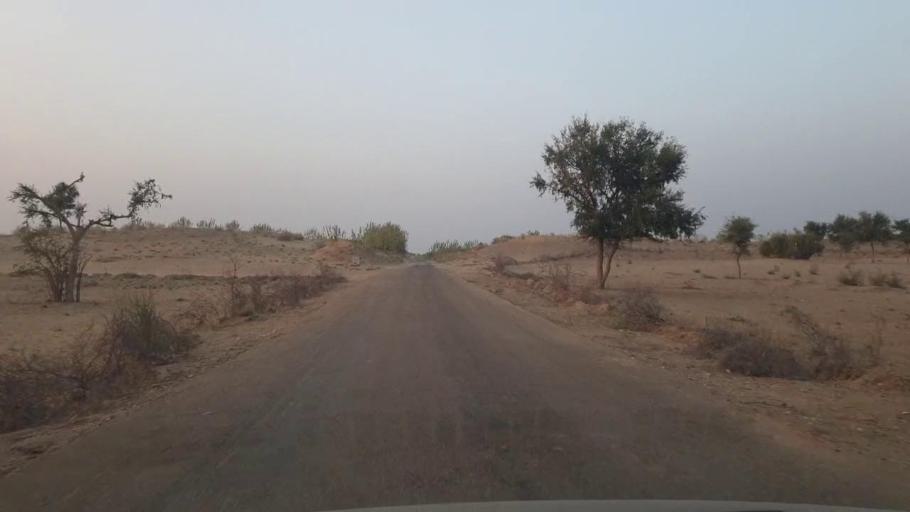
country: PK
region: Sindh
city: Umarkot
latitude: 25.2734
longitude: 70.0773
